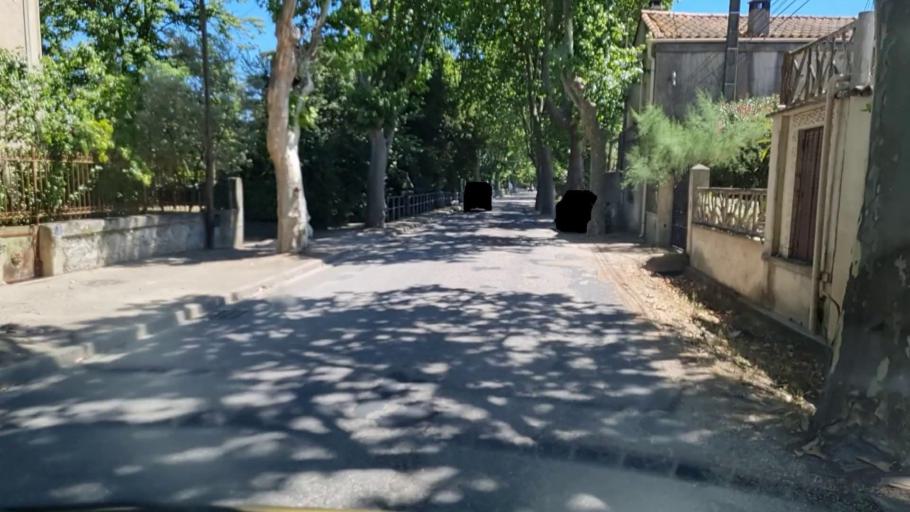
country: FR
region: Languedoc-Roussillon
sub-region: Departement du Gard
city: Le Cailar
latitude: 43.6823
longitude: 4.2344
